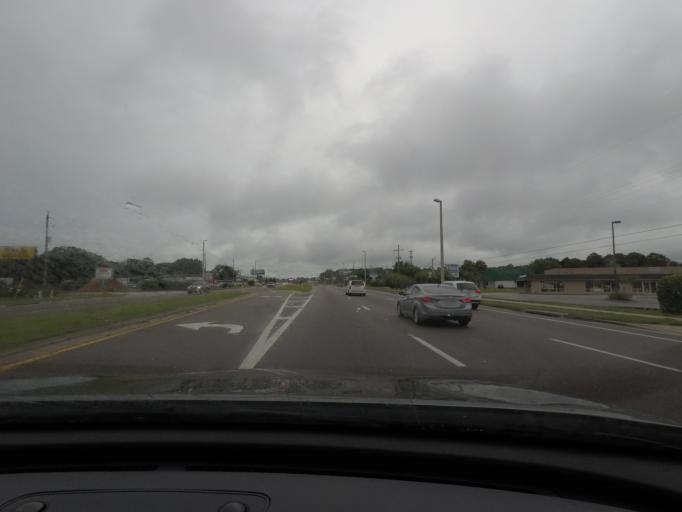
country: US
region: Florida
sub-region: Orange County
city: Union Park
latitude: 28.5662
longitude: -81.2964
